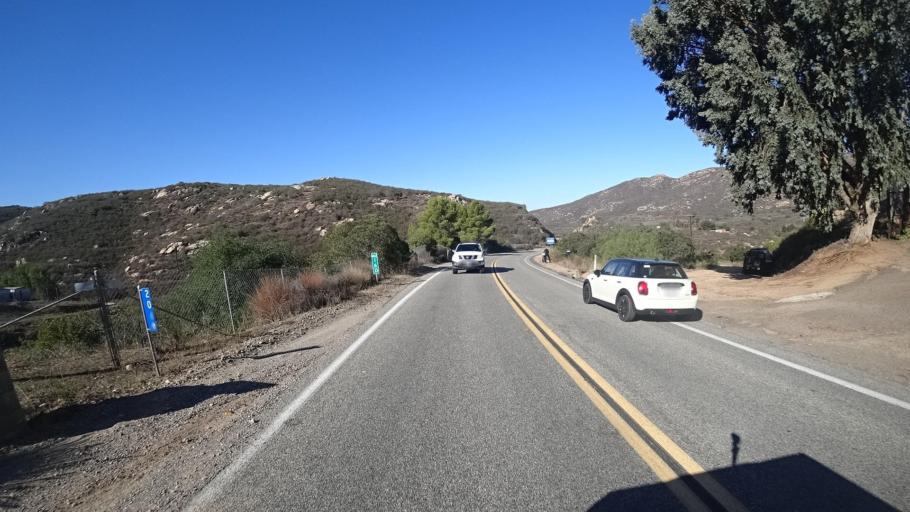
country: US
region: California
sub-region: San Diego County
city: Jamul
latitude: 32.6724
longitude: -116.7757
